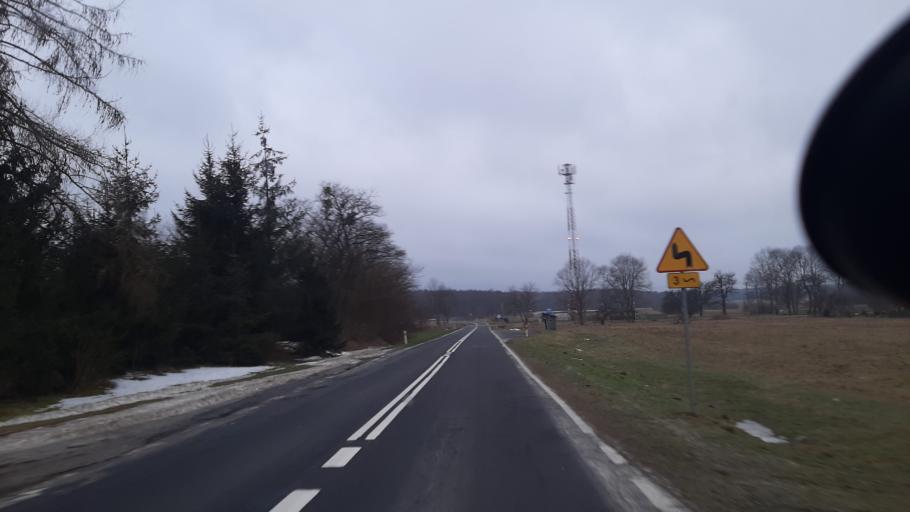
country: PL
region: Lublin Voivodeship
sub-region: Powiat wlodawski
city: Hansk
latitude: 51.5590
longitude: 23.3115
